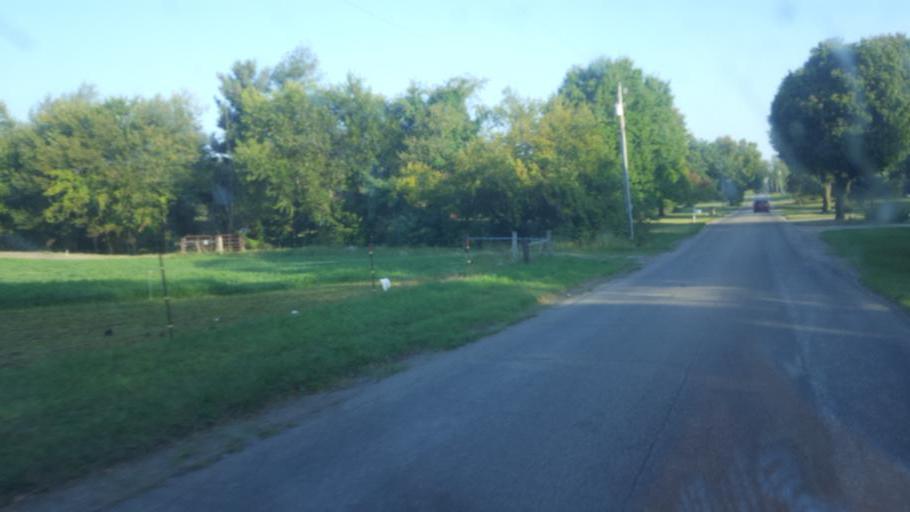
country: US
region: Indiana
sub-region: LaGrange County
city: Lagrange
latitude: 41.6337
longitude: -85.4247
